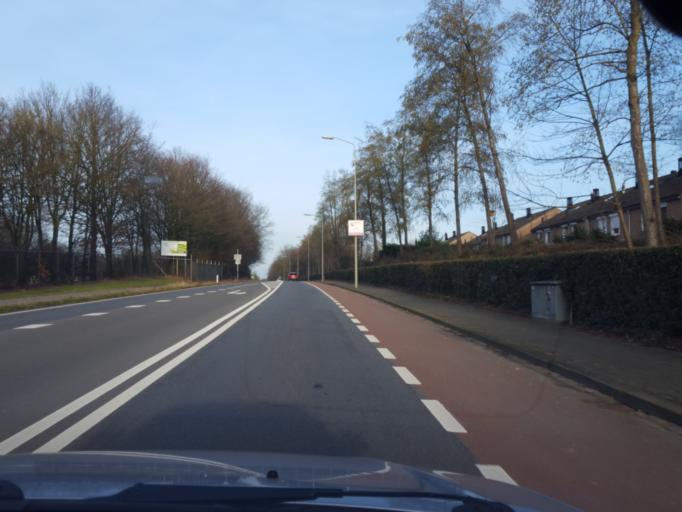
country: NL
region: Limburg
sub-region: Gemeente Heerlen
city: Hoensbroek
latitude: 50.9237
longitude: 5.9110
